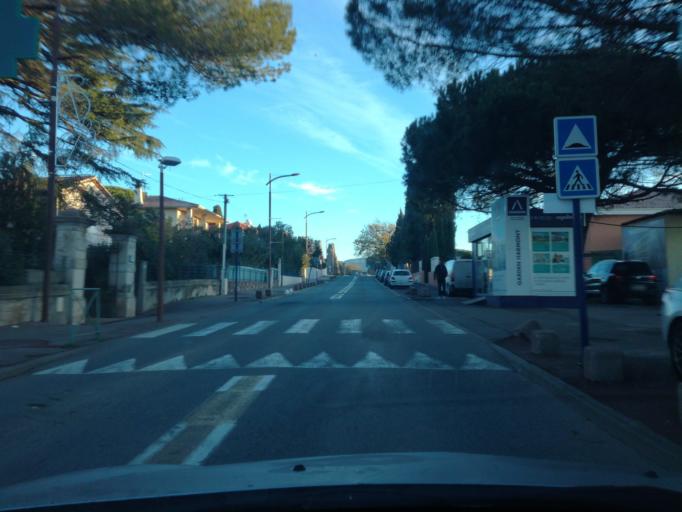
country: FR
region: Provence-Alpes-Cote d'Azur
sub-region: Departement du Var
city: Frejus
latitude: 43.4363
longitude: 6.7399
